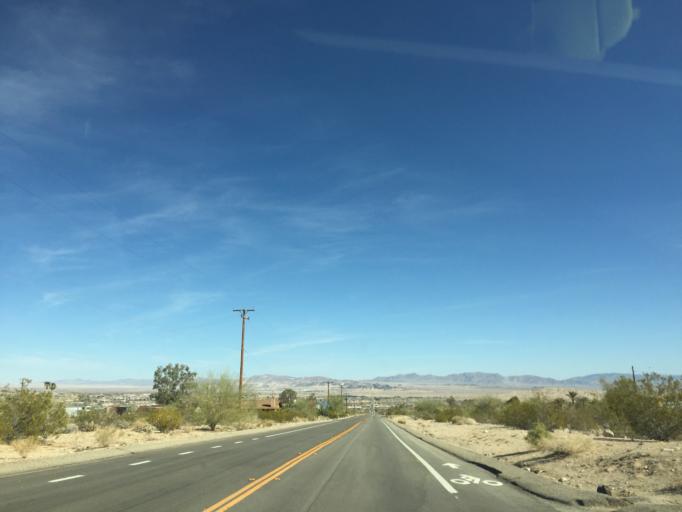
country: US
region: California
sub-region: San Bernardino County
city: Twentynine Palms
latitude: 34.1103
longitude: -116.0367
